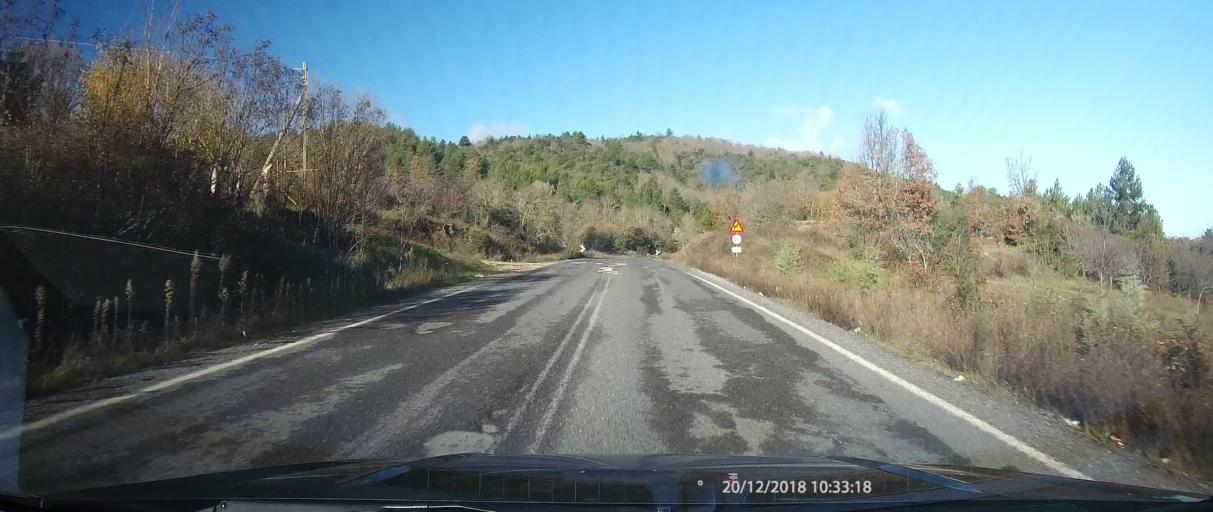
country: GR
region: Peloponnese
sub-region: Nomos Lakonias
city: Kariai
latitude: 37.3368
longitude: 22.4167
